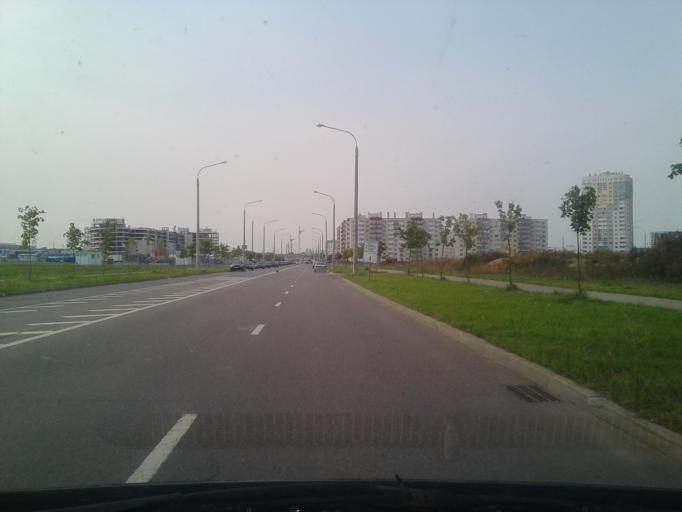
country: BY
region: Minsk
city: Zhdanovichy
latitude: 53.9321
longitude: 27.4662
